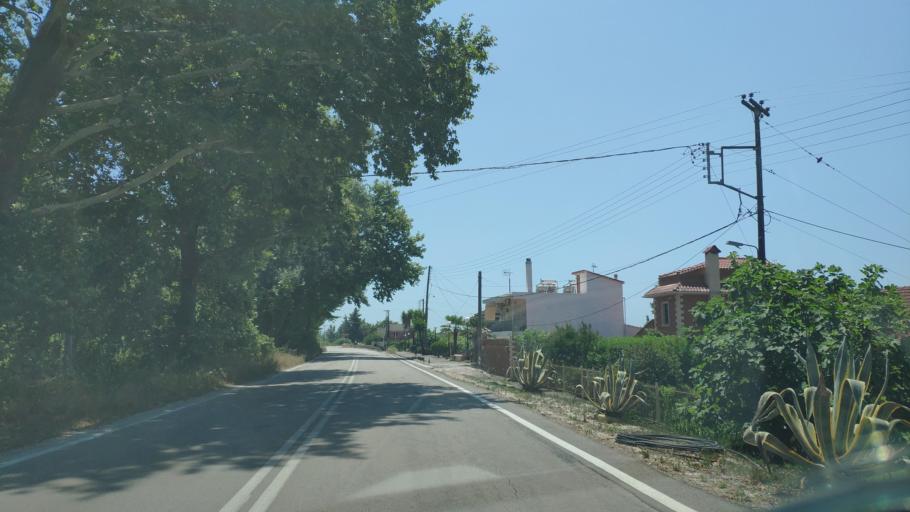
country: GR
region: Epirus
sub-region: Nomos Artas
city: Neochori
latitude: 39.0866
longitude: 21.0154
